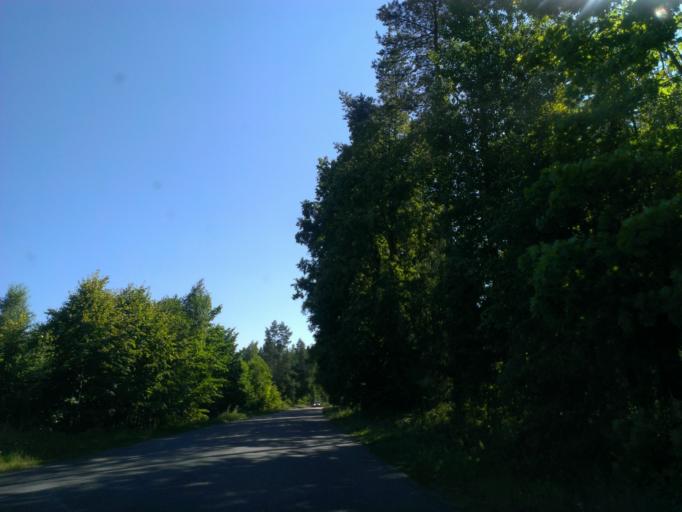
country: LV
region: Sigulda
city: Sigulda
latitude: 57.1095
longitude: 24.8256
